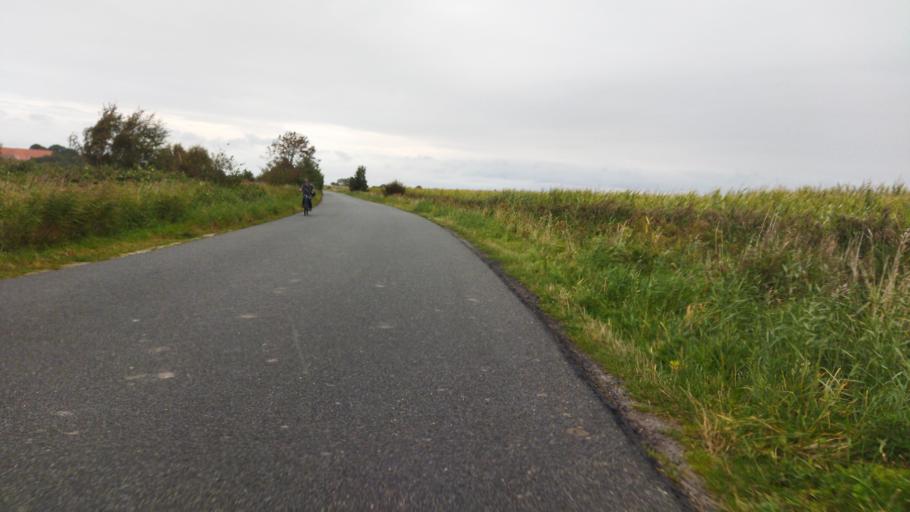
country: DE
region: Lower Saxony
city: Wirdum
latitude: 53.4986
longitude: 7.0557
